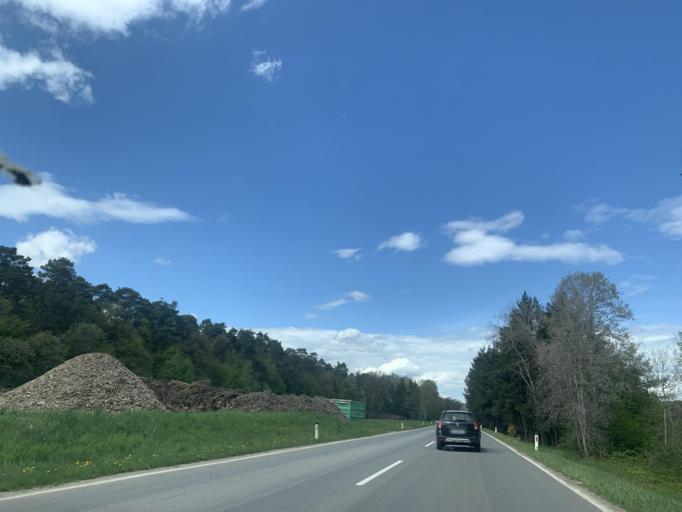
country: AT
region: Styria
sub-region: Politischer Bezirk Leibnitz
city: Lang
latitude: 46.8238
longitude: 15.5228
